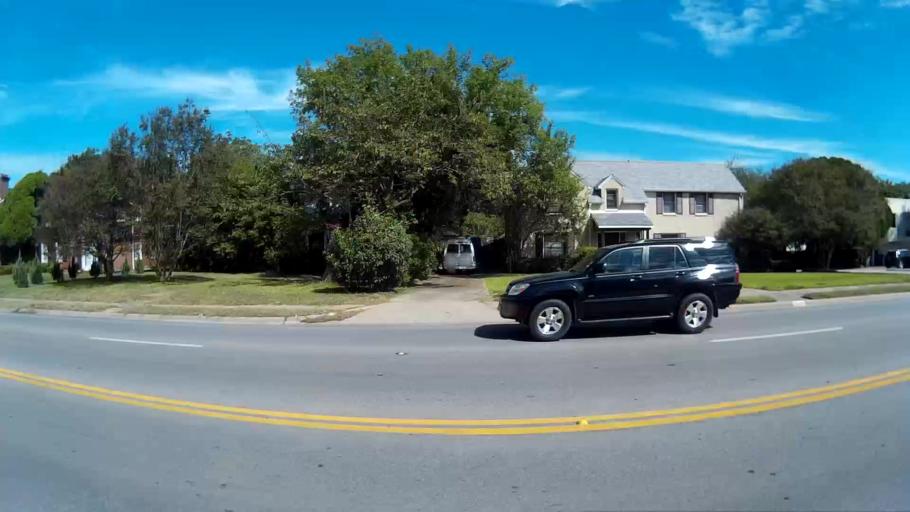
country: US
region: Texas
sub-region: Dallas County
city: Highland Park
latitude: 32.8160
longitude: -96.7424
